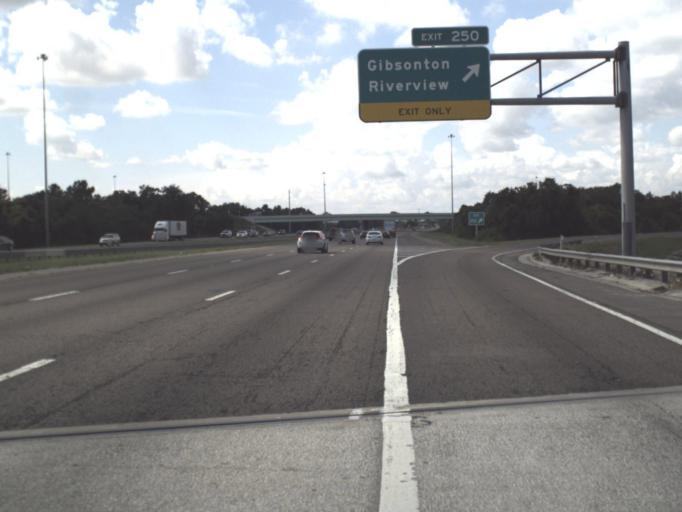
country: US
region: Florida
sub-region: Hillsborough County
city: Riverview
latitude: 27.8559
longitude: -82.3469
